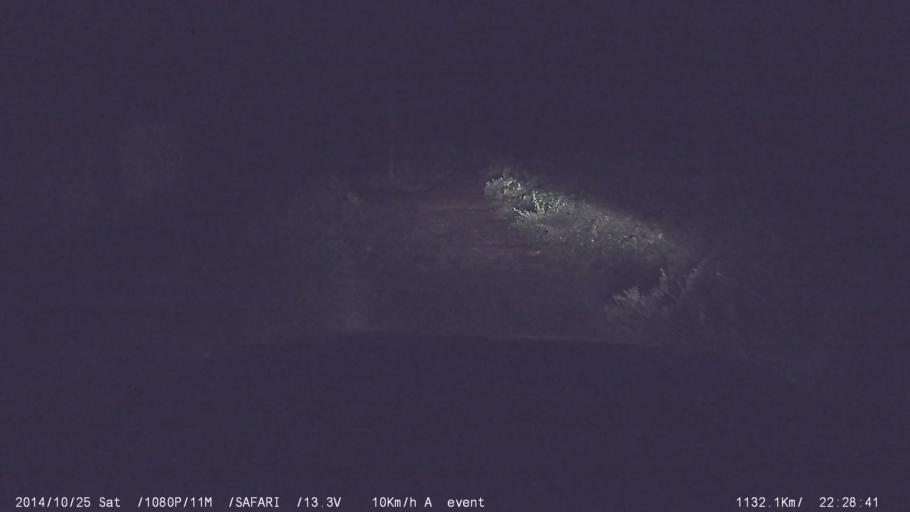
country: IN
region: Kerala
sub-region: Kottayam
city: Palackattumala
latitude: 9.7884
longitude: 76.5635
